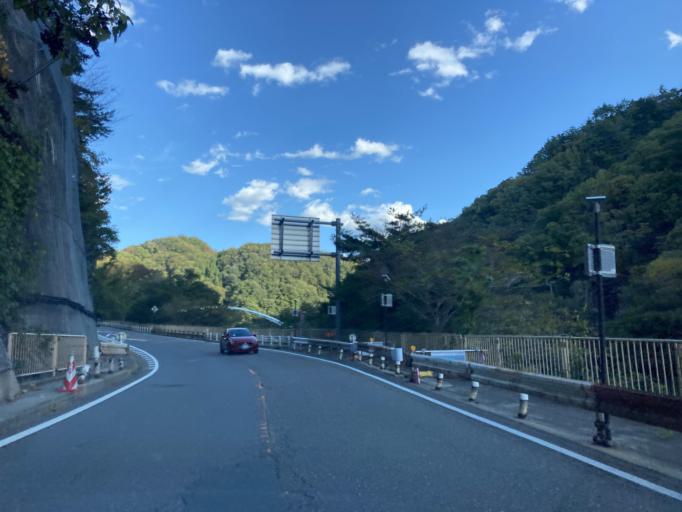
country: JP
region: Nagano
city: Omachi
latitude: 36.4650
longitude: 137.9561
